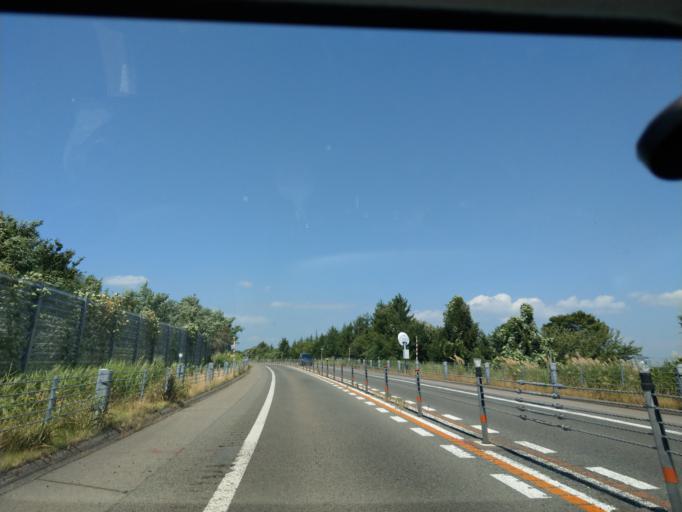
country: JP
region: Akita
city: Yokotemachi
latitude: 39.3425
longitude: 140.5007
